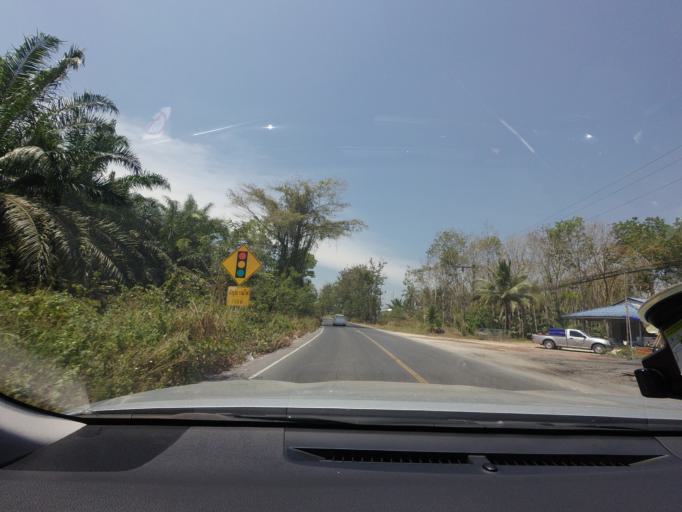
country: TH
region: Surat Thani
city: Tha Chang
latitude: 9.2672
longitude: 99.1543
